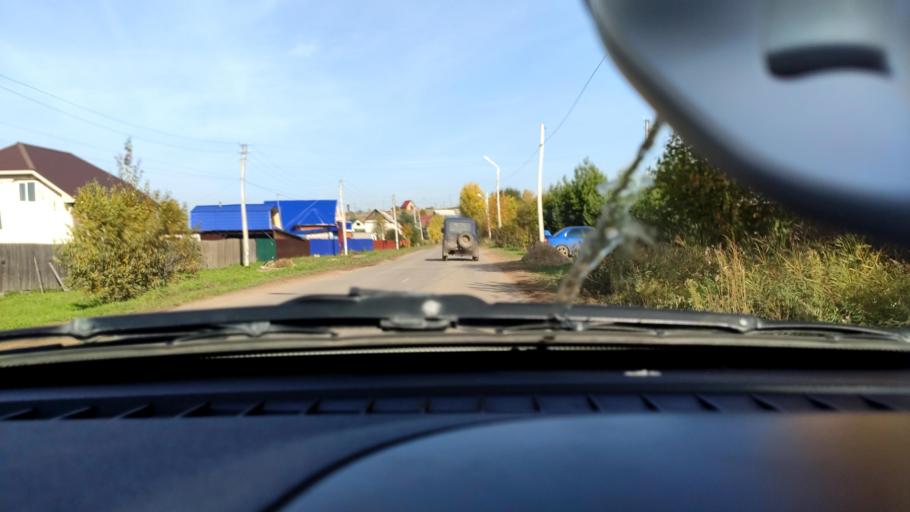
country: RU
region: Perm
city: Overyata
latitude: 58.0750
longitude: 55.8874
